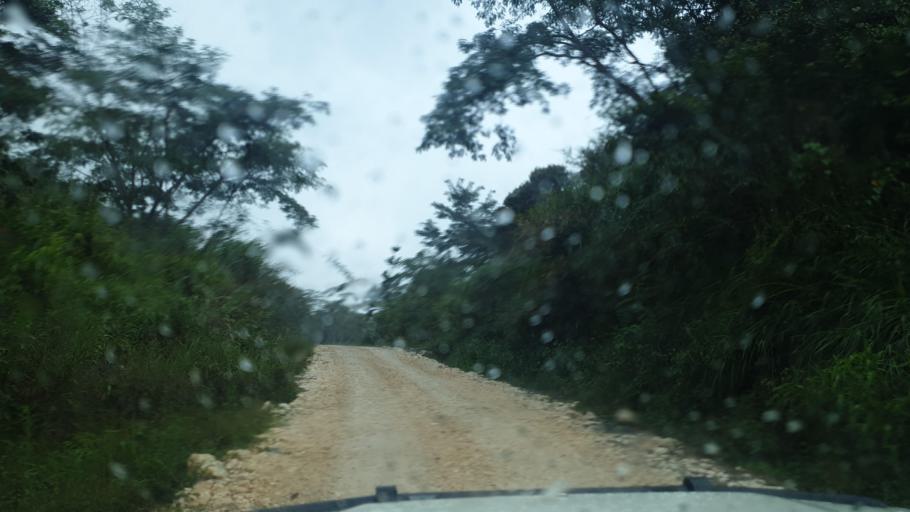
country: PG
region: Eastern Highlands
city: Goroka
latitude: -6.1980
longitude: 145.2134
